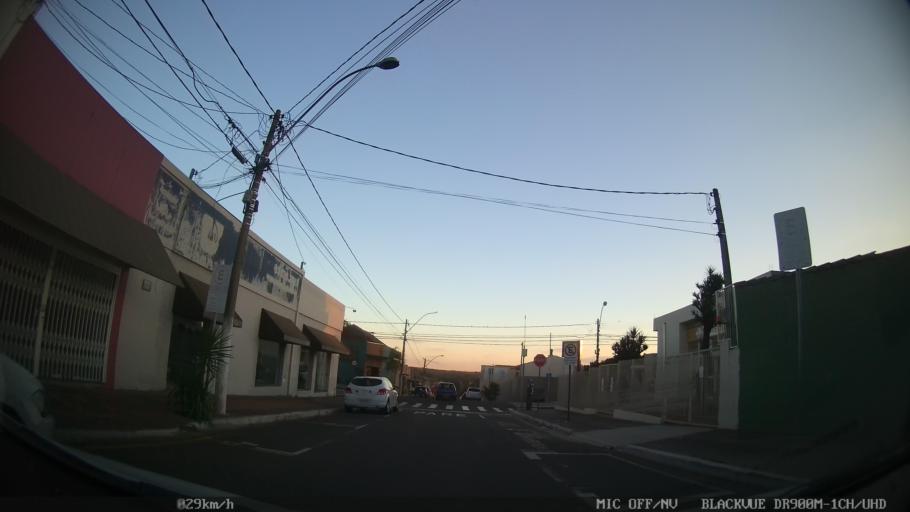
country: BR
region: Sao Paulo
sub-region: Santa Barbara D'Oeste
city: Santa Barbara d'Oeste
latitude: -22.7571
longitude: -47.4153
